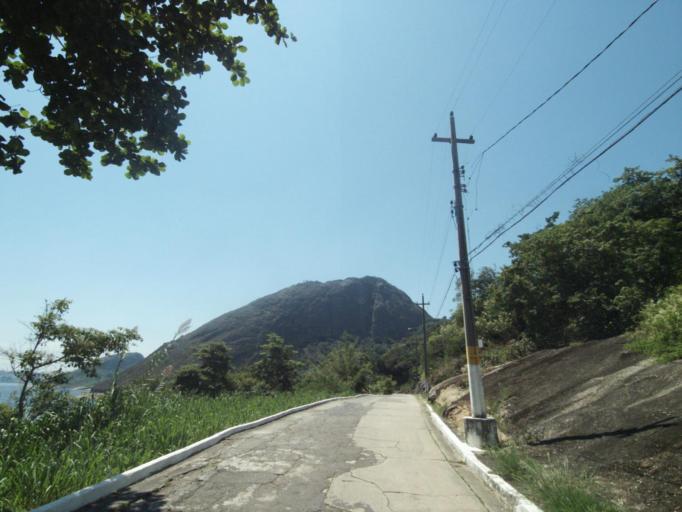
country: BR
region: Rio de Janeiro
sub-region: Niteroi
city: Niteroi
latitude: -22.9372
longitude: -43.1295
